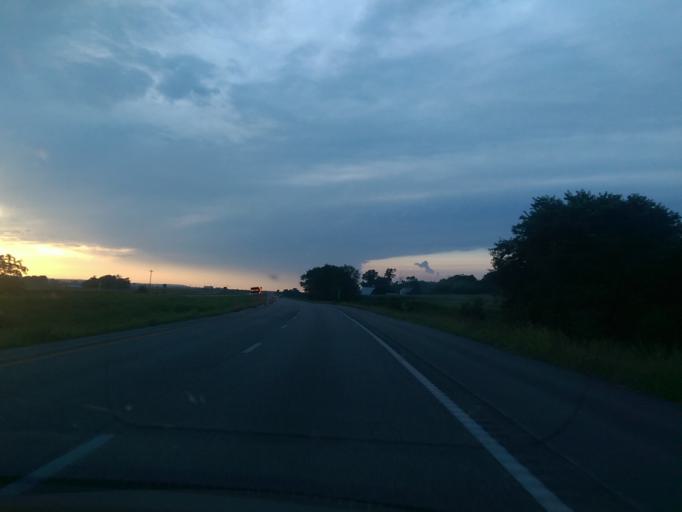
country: US
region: Missouri
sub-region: Atchison County
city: Rock Port
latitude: 40.3575
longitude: -95.5178
